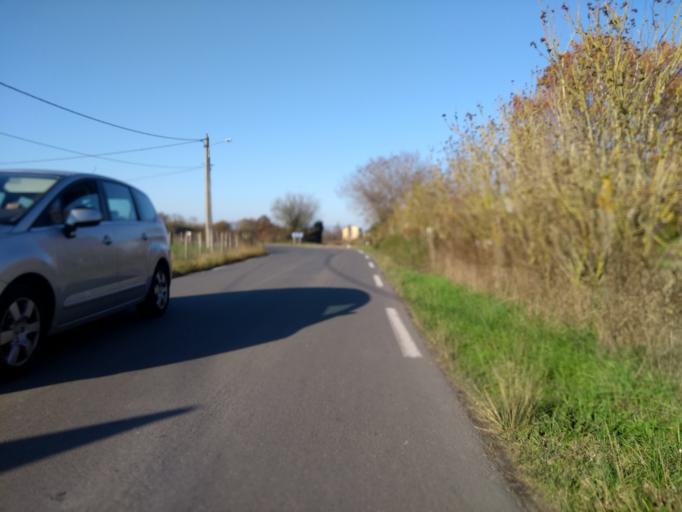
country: FR
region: Aquitaine
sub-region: Departement de la Gironde
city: Martillac
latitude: 44.7279
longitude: -0.5119
